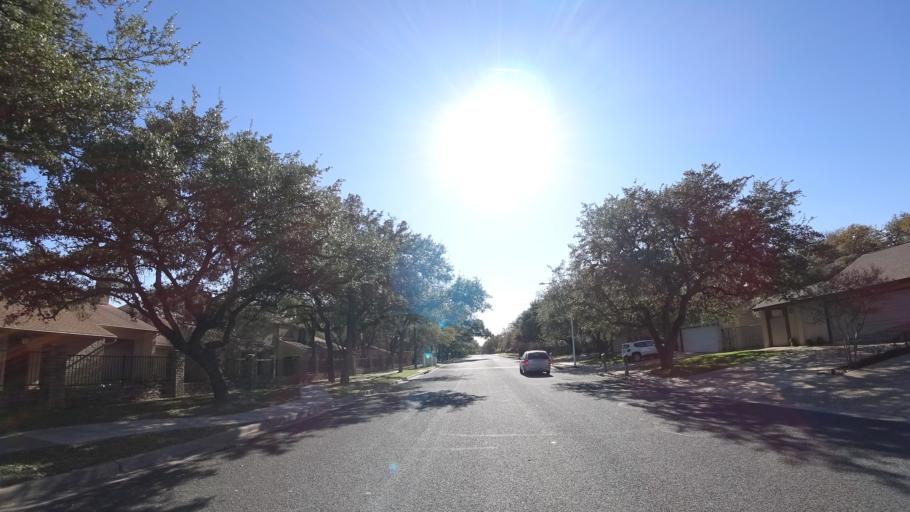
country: US
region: Texas
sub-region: Williamson County
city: Jollyville
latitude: 30.3722
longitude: -97.7498
